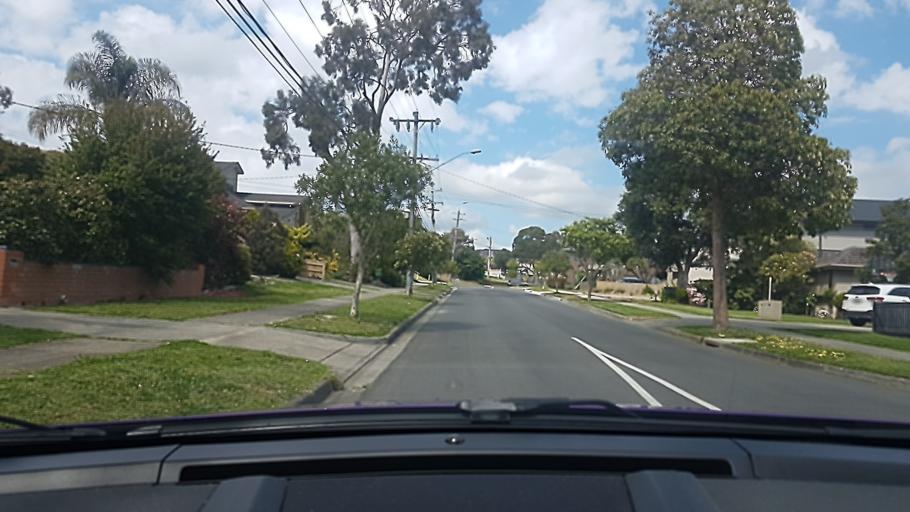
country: AU
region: Victoria
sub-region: Banyule
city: Darch
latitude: -37.7580
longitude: 145.1054
